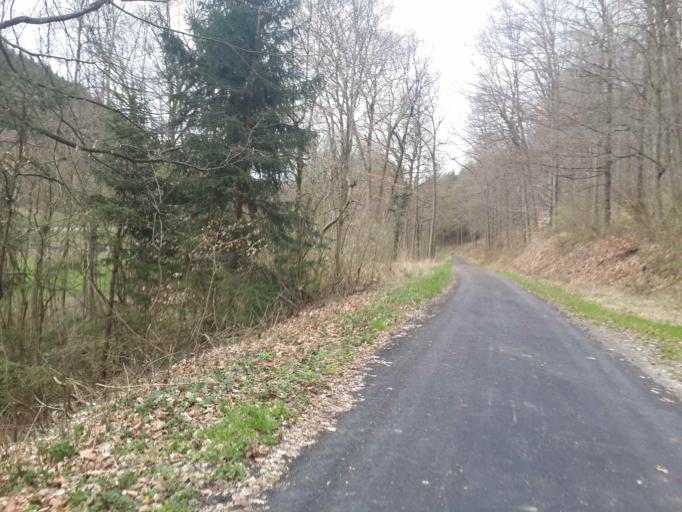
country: DE
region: Baden-Wuerttemberg
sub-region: Karlsruhe Region
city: Billigheim
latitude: 49.3321
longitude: 9.2489
